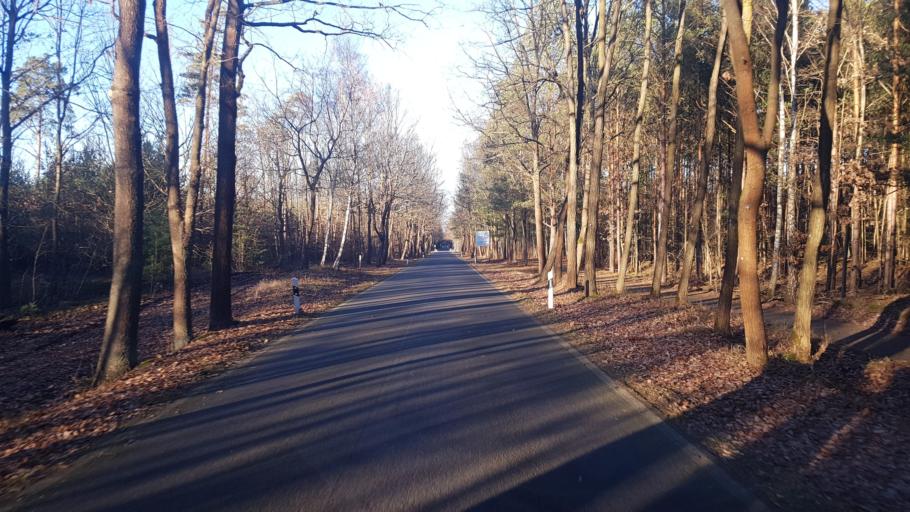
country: DE
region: Brandenburg
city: Tauer
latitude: 51.9171
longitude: 14.4902
